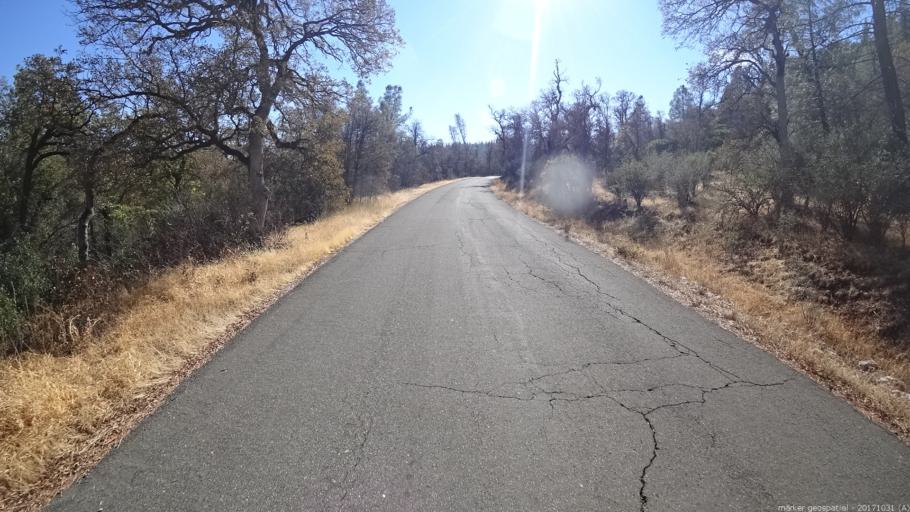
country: US
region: California
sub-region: Shasta County
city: Shingletown
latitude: 40.5278
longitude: -121.9267
